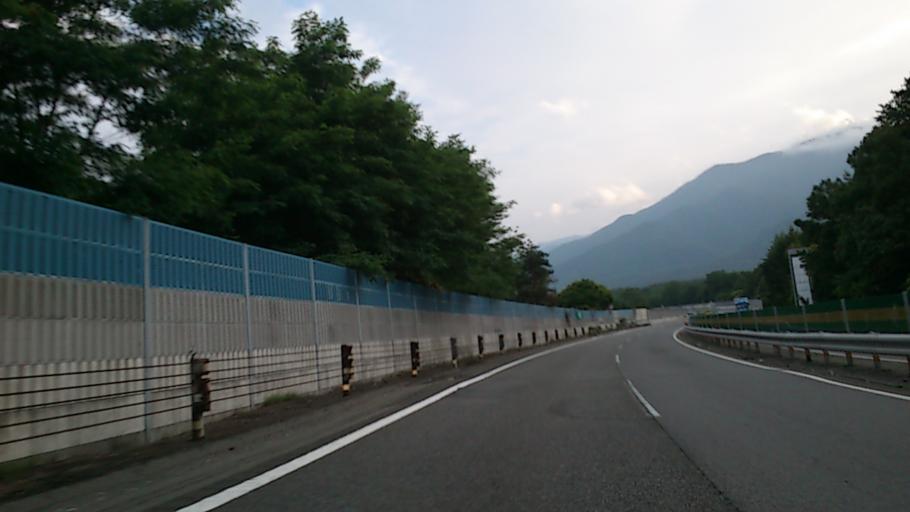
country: JP
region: Nagano
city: Ina
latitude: 35.7561
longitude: 137.9161
